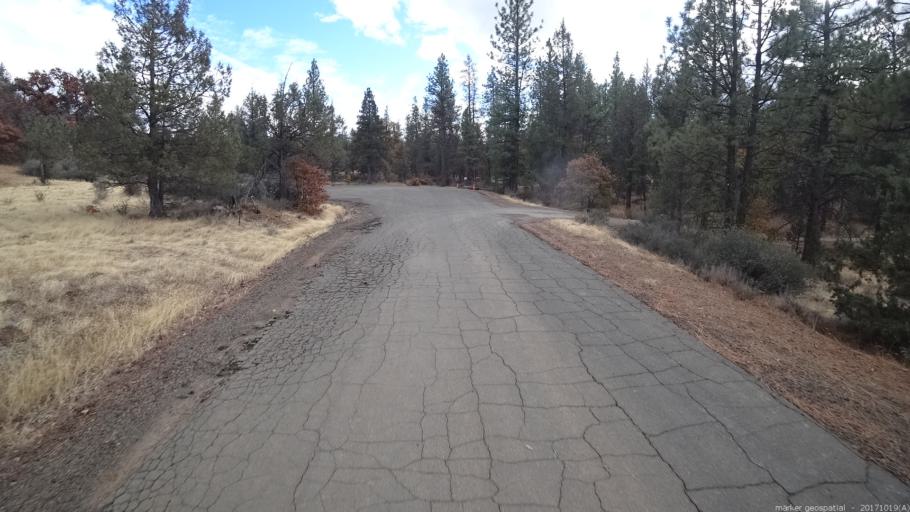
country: US
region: California
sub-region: Shasta County
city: Burney
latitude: 40.9724
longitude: -121.4459
